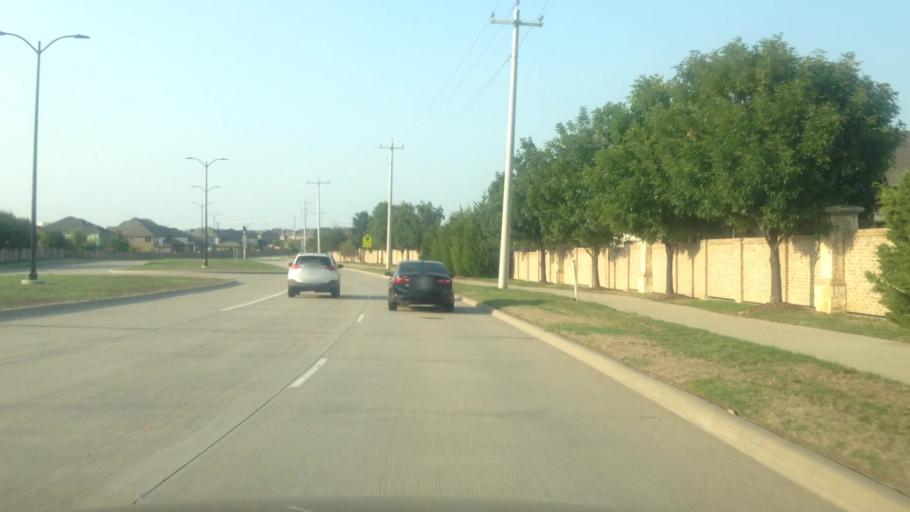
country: US
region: Texas
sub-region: Denton County
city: The Colony
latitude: 33.1179
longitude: -96.8848
